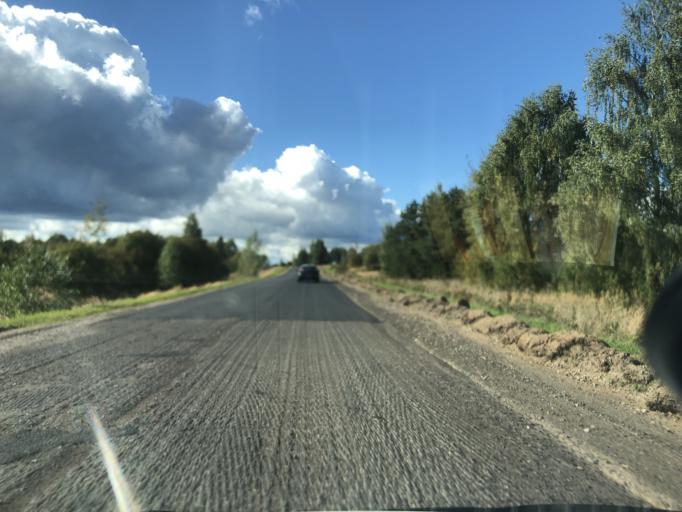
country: RU
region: Jaroslavl
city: Petrovsk
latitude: 56.9606
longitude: 39.3716
